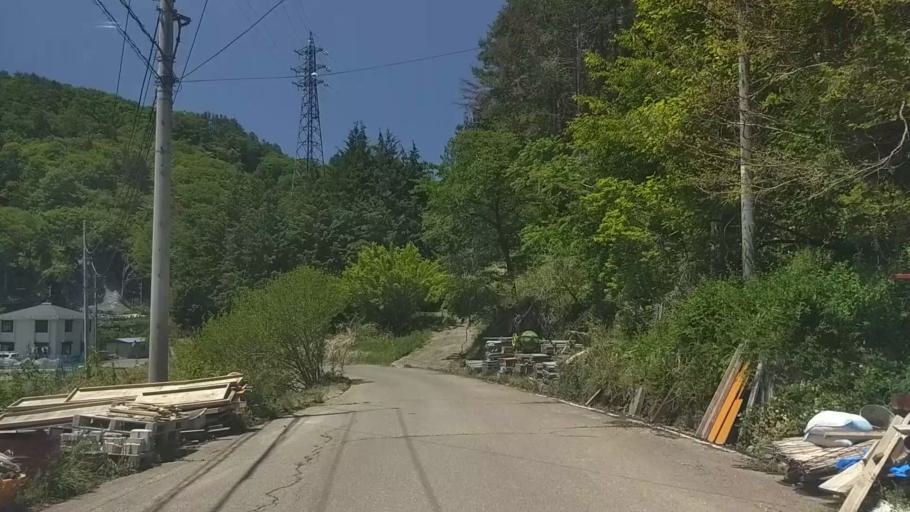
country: JP
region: Yamanashi
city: Nirasaki
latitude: 35.8770
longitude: 138.4308
